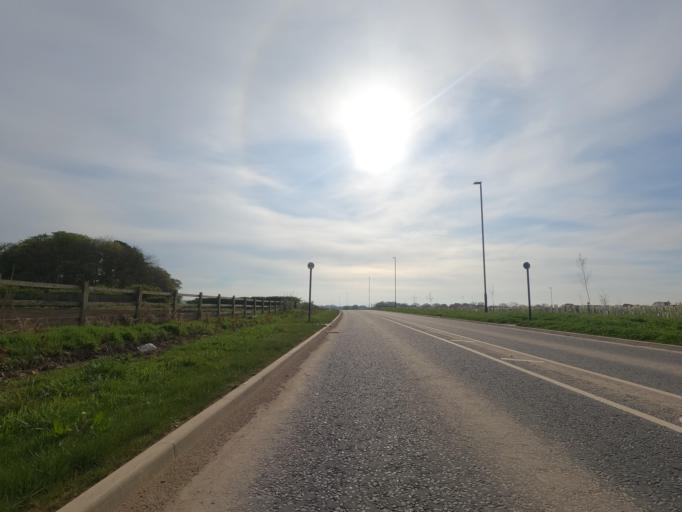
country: GB
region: England
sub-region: Newcastle upon Tyne
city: Hazlerigg
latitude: 55.0335
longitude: -1.6588
